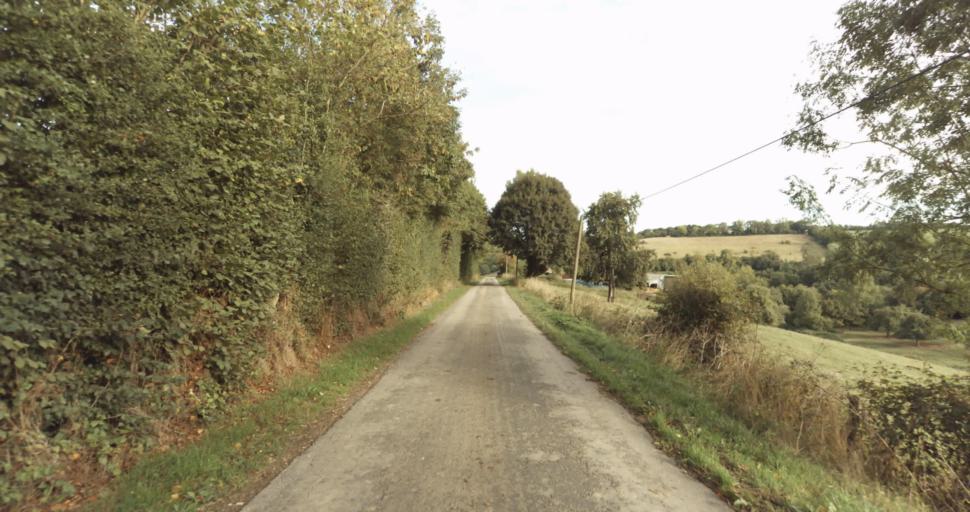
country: FR
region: Lower Normandy
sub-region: Departement de l'Orne
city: Vimoutiers
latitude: 48.8681
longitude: 0.2448
